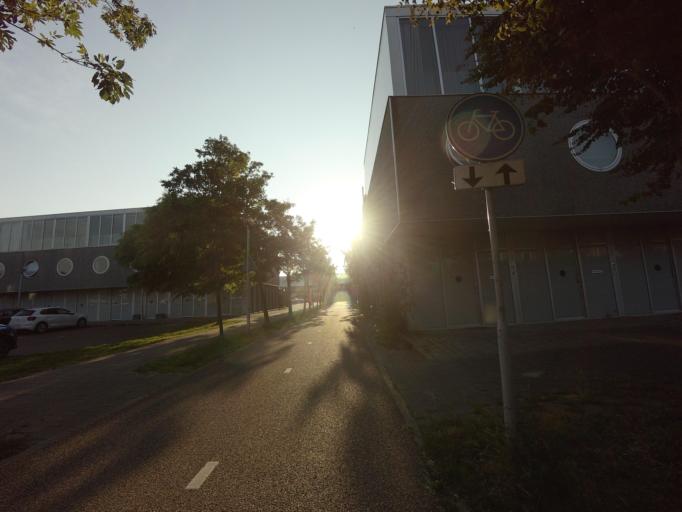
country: NL
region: Utrecht
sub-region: Stichtse Vecht
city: Spechtenkamp
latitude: 52.0955
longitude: 5.0046
